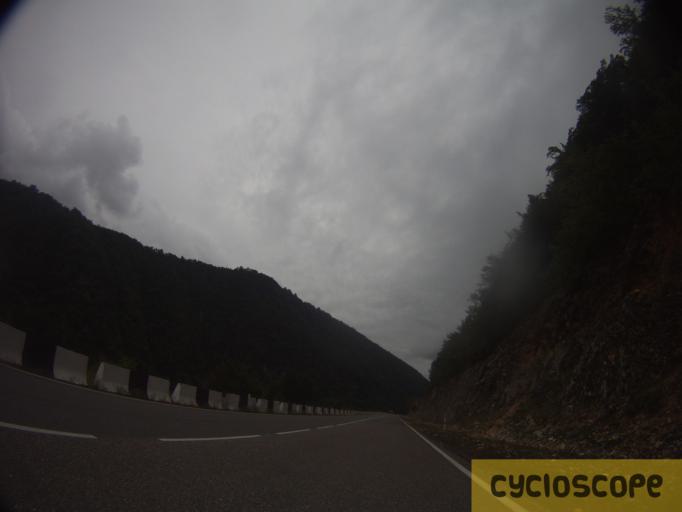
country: GE
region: Samegrelo and Zemo Svaneti
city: Jvari
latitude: 42.7882
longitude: 42.0526
